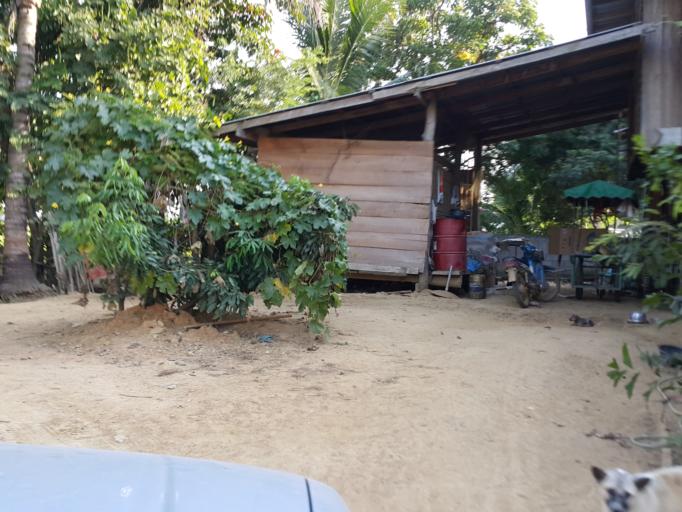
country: TH
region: Sukhothai
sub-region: Amphoe Si Satchanalai
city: Si Satchanalai
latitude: 17.4766
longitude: 99.6472
